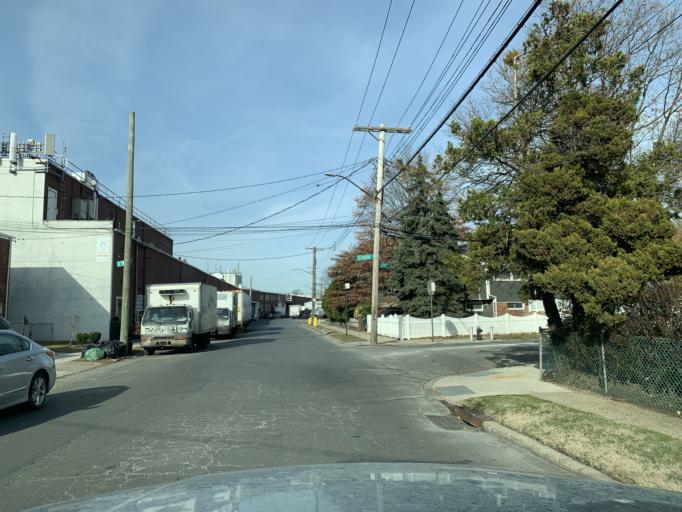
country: US
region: New York
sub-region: Queens County
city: Jamaica
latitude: 40.6976
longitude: -73.7701
